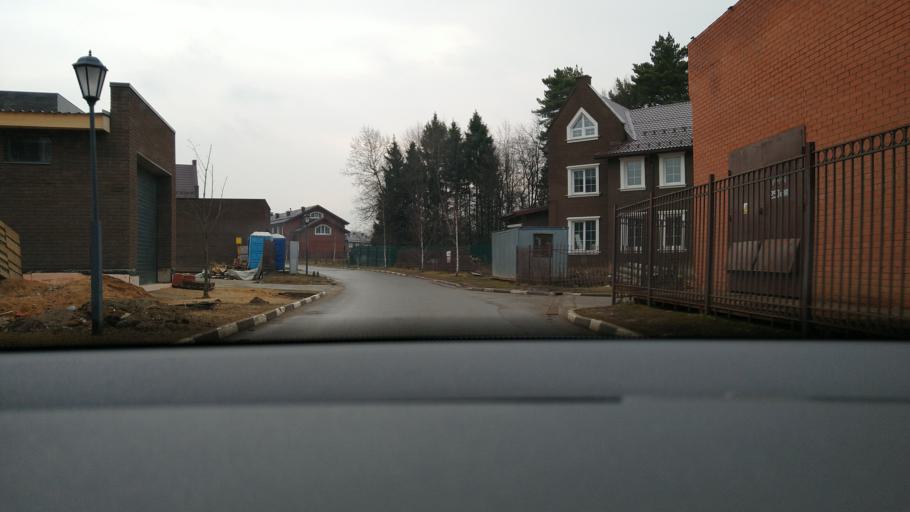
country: RU
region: Moskovskaya
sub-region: Leninskiy Rayon
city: Vnukovo
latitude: 55.6176
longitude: 37.3195
